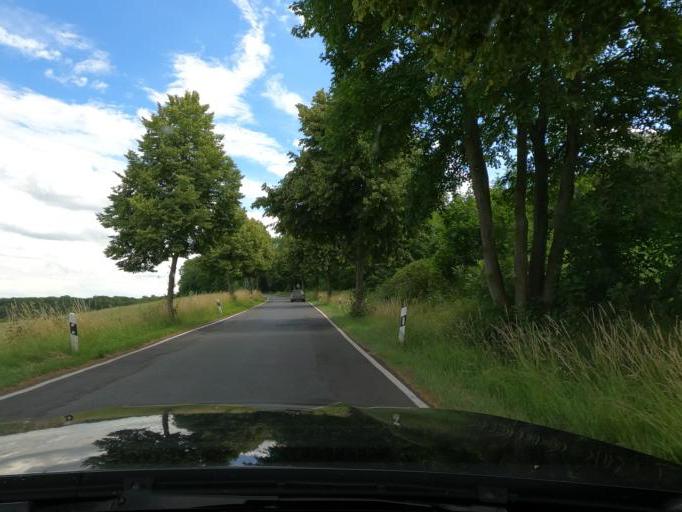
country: DE
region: Lower Saxony
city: Elbe
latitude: 52.1227
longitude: 10.2942
